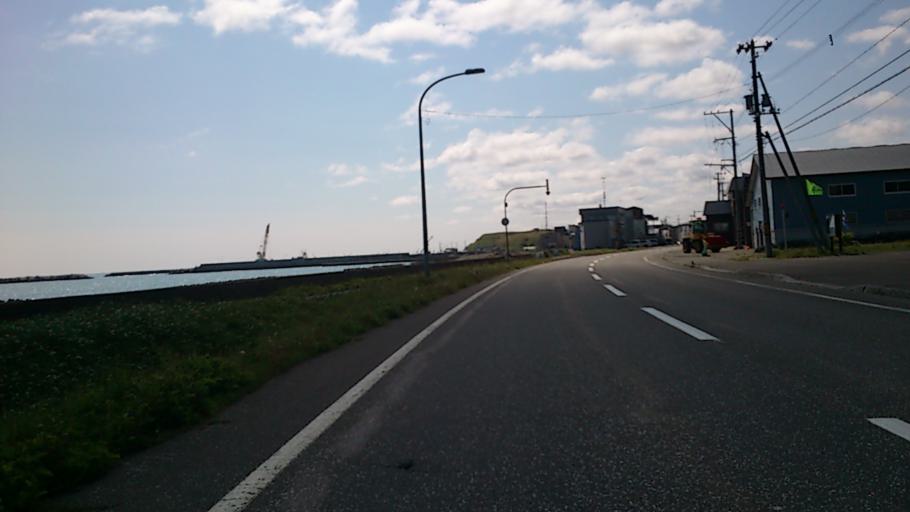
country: JP
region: Hokkaido
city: Makubetsu
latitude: 45.3834
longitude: 142.0843
